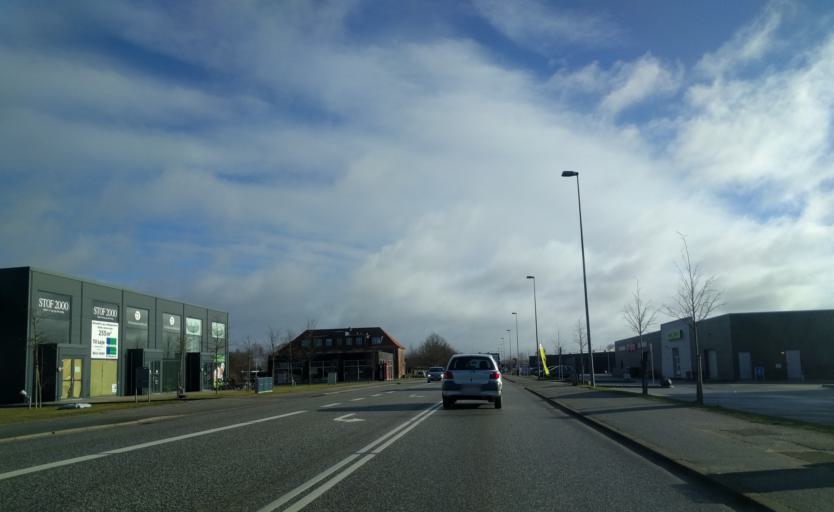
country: DK
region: North Denmark
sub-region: Alborg Kommune
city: Svenstrup
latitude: 57.0063
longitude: 9.8767
